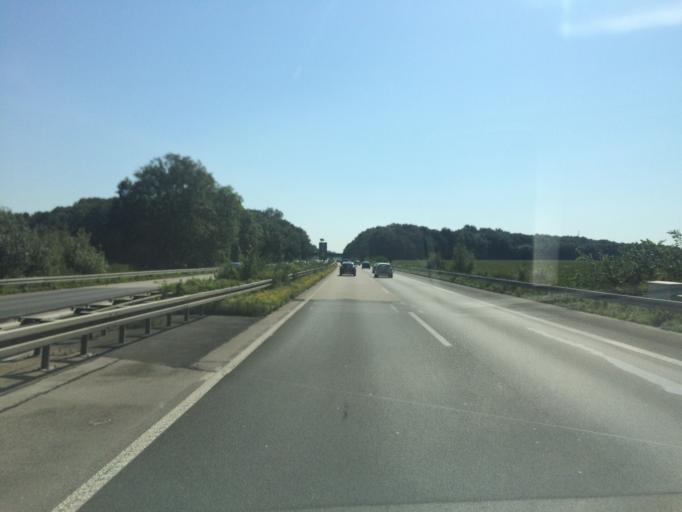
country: DE
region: North Rhine-Westphalia
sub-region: Regierungsbezirk Munster
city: Ascheberg
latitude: 51.8336
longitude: 7.5942
